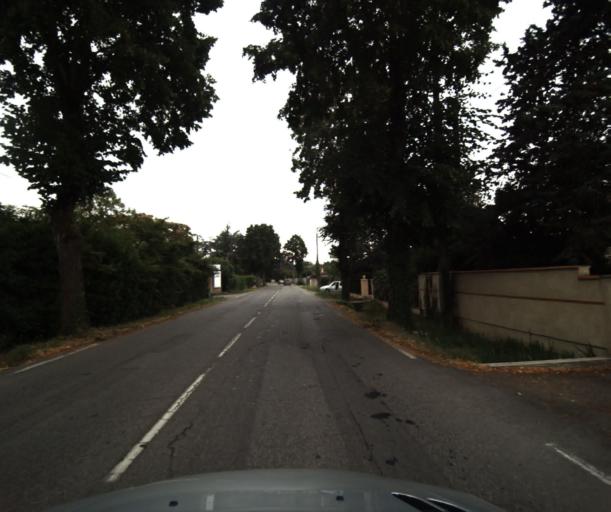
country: FR
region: Midi-Pyrenees
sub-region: Departement de la Haute-Garonne
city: Pinsaguel
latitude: 43.5165
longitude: 1.3874
